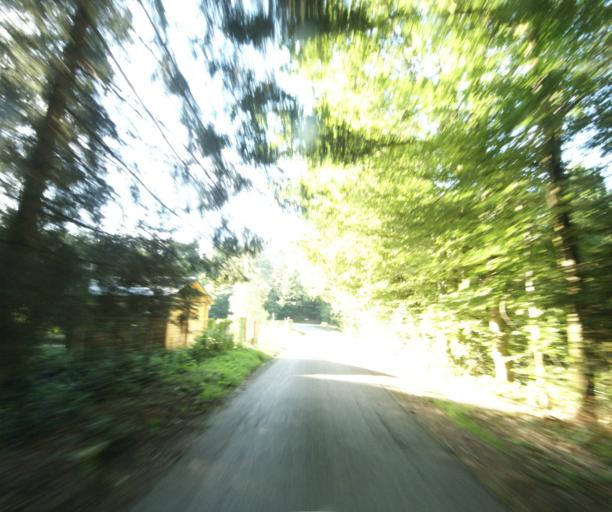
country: FR
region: Lorraine
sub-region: Departement des Vosges
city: Urimenil
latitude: 48.1355
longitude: 6.4138
